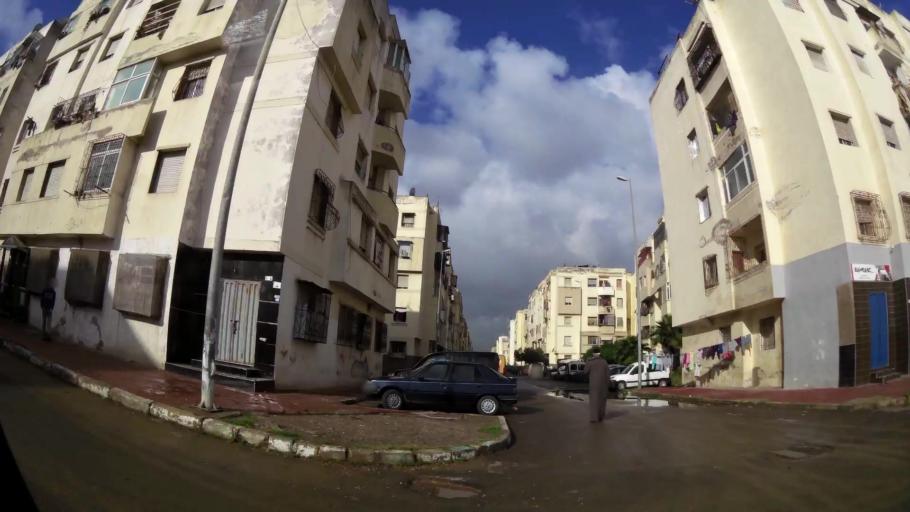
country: MA
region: Grand Casablanca
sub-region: Mediouna
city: Tit Mellil
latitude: 33.5967
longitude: -7.5378
